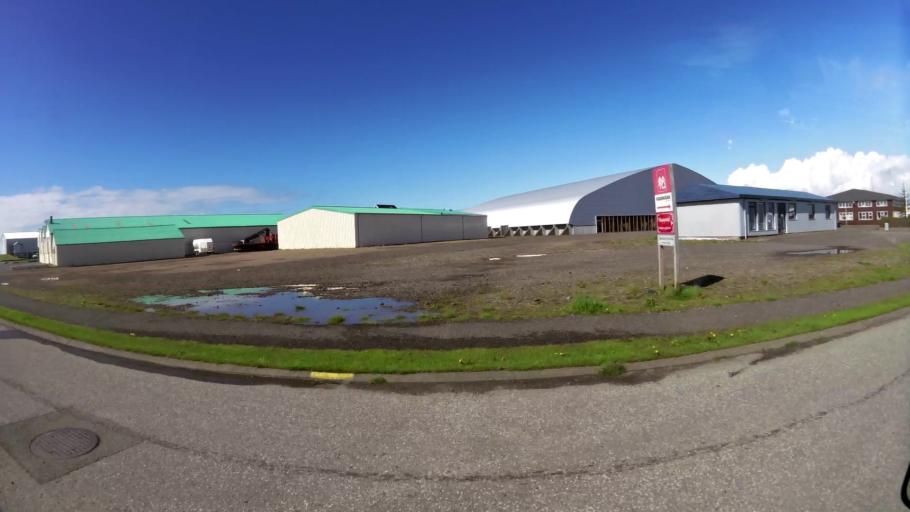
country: IS
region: East
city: Hoefn
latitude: 64.2518
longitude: -15.2028
